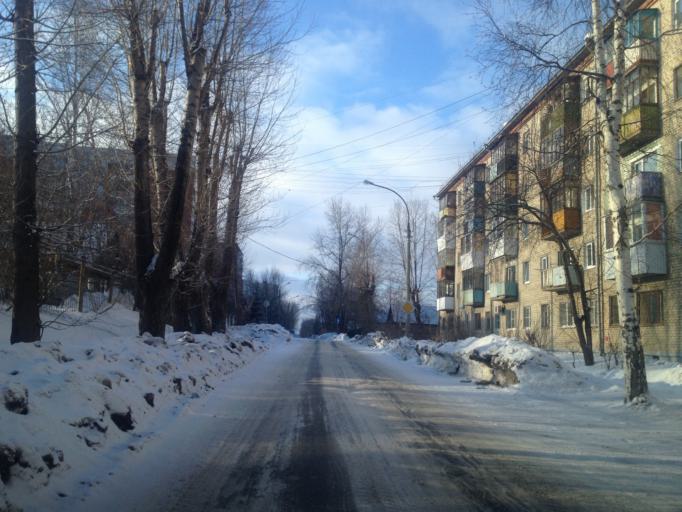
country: RU
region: Sverdlovsk
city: Sovkhoznyy
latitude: 56.7693
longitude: 60.5995
